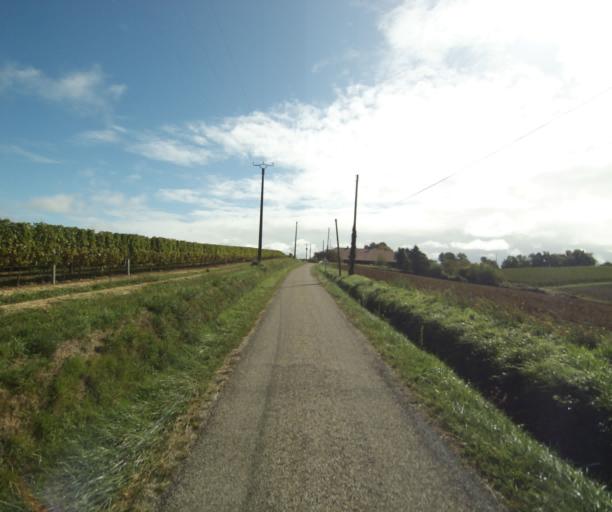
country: FR
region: Midi-Pyrenees
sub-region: Departement du Gers
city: Cazaubon
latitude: 43.8536
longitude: -0.0585
